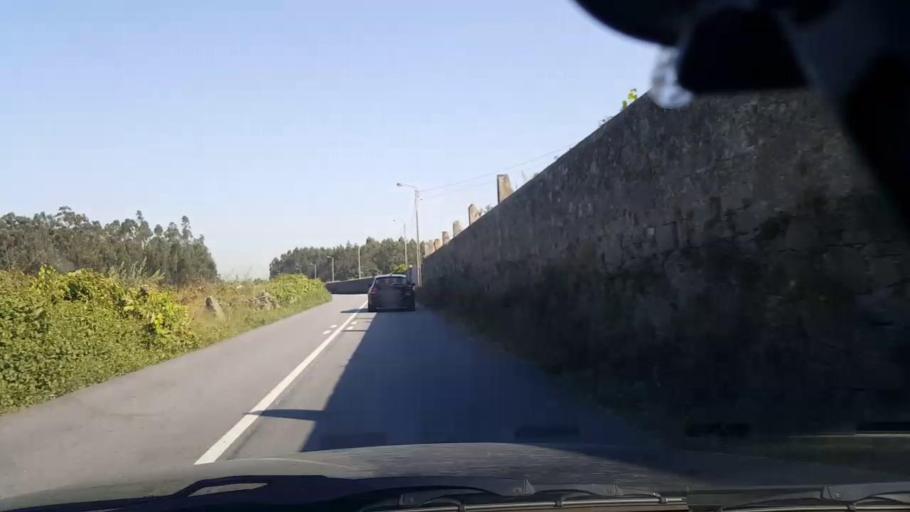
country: PT
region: Porto
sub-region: Vila do Conde
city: Arvore
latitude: 41.3286
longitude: -8.6803
